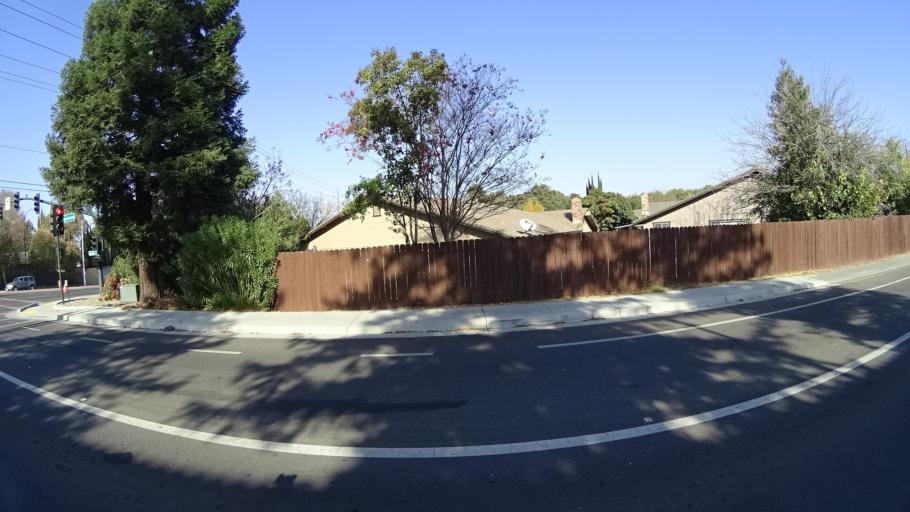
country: US
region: California
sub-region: Sacramento County
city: Citrus Heights
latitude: 38.6954
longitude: -121.2713
